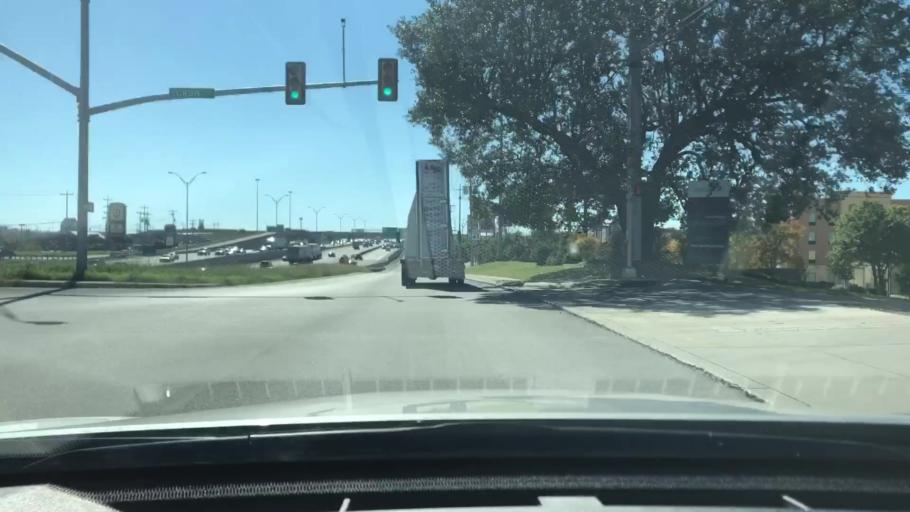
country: US
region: Texas
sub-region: Bexar County
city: Live Oak
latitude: 29.5729
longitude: -98.3280
